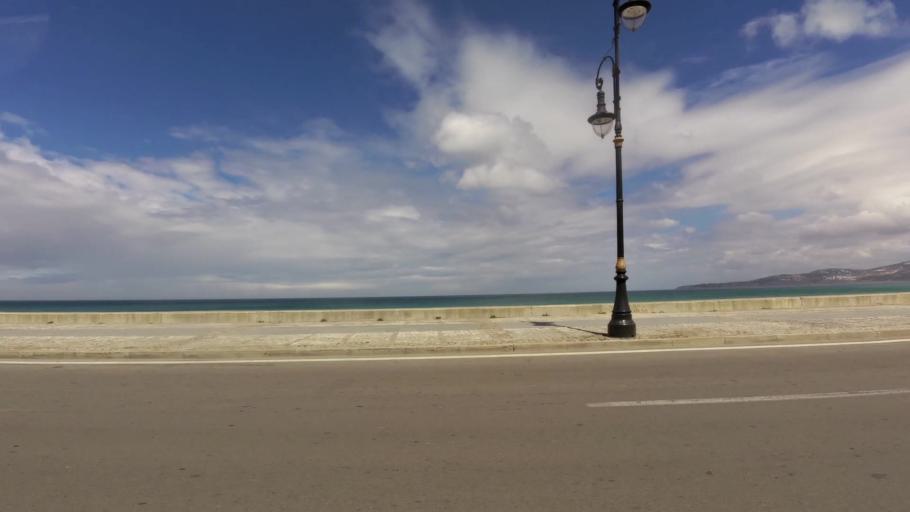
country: MA
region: Tanger-Tetouan
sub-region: Tanger-Assilah
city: Tangier
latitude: 35.7934
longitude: -5.8233
